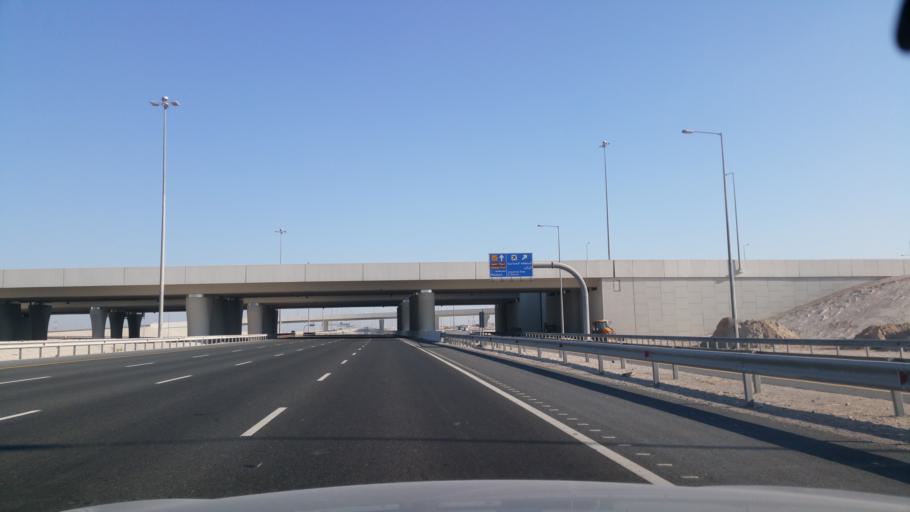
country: QA
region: Al Wakrah
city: Al Wukayr
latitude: 25.1236
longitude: 51.4861
